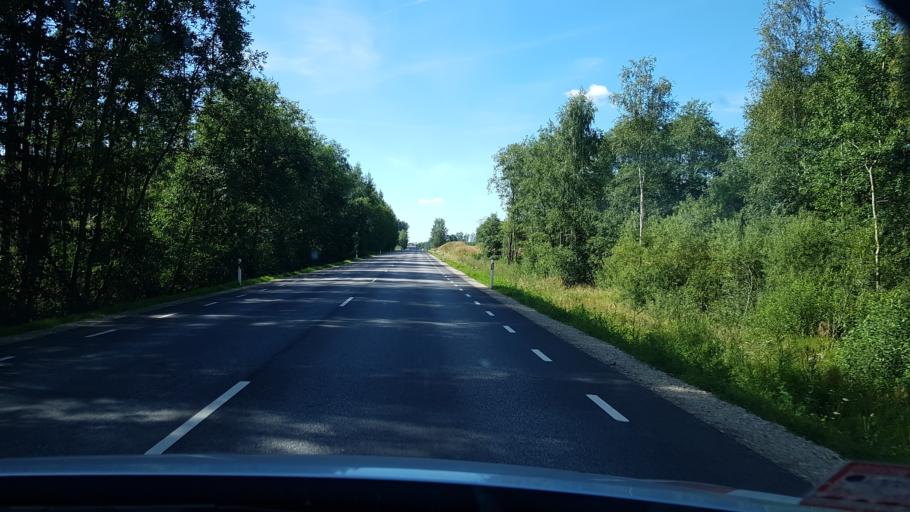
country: EE
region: Polvamaa
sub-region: Polva linn
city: Polva
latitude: 58.0414
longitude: 27.1063
